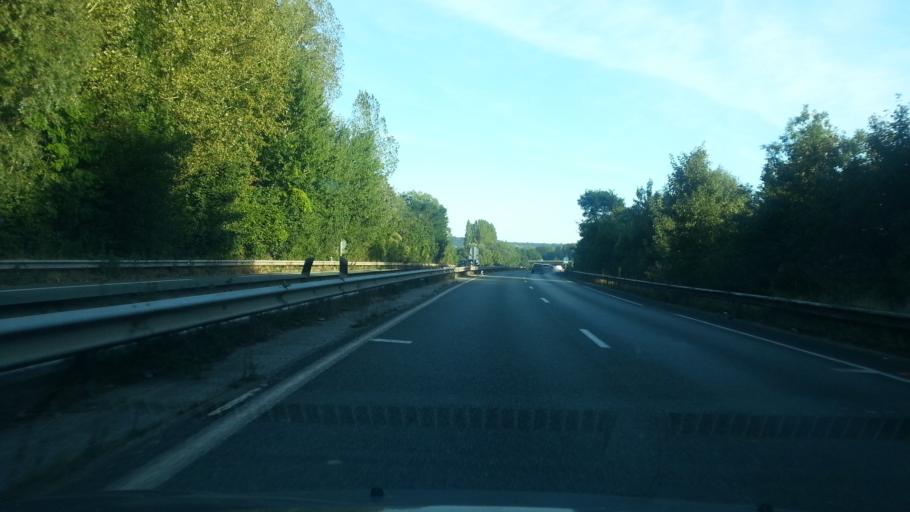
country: FR
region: Picardie
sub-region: Departement de l'Oise
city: Fitz-James
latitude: 49.3861
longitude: 2.4282
